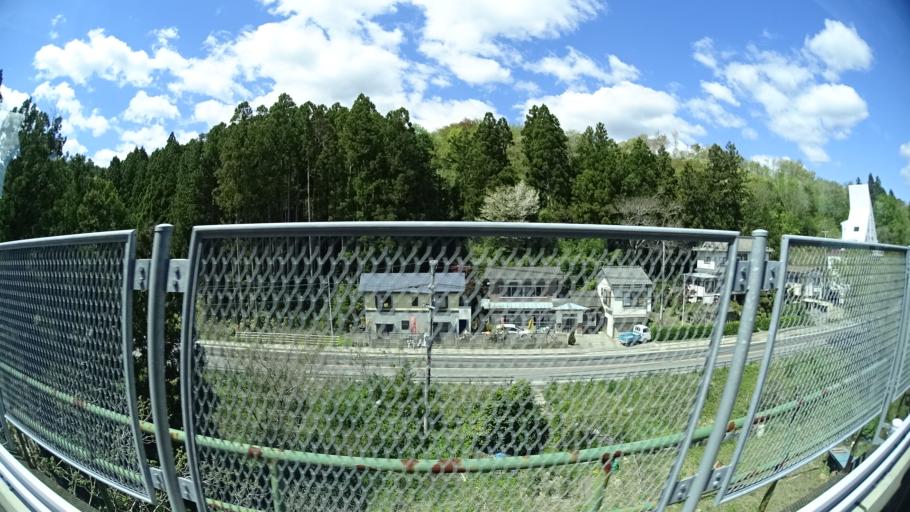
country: JP
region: Miyagi
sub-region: Oshika Gun
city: Onagawa Cho
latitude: 38.6628
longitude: 141.4457
